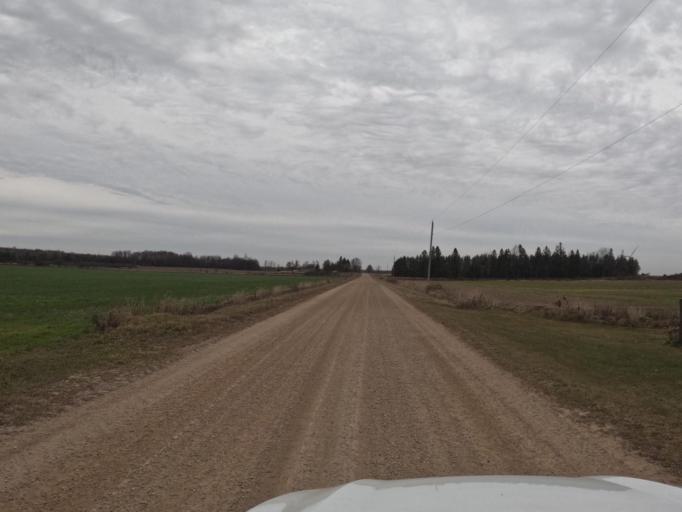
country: CA
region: Ontario
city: Shelburne
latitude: 44.0214
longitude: -80.3693
